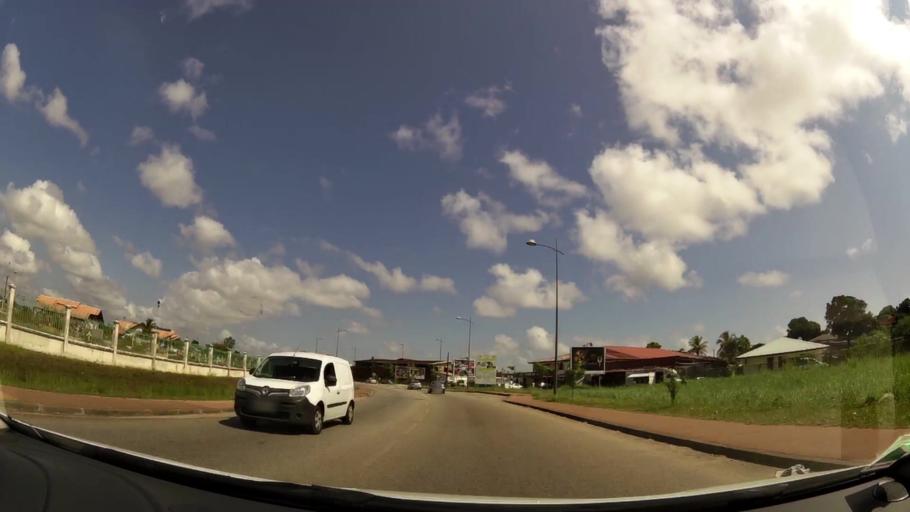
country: GF
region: Guyane
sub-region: Guyane
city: Cayenne
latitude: 4.9169
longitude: -52.3122
